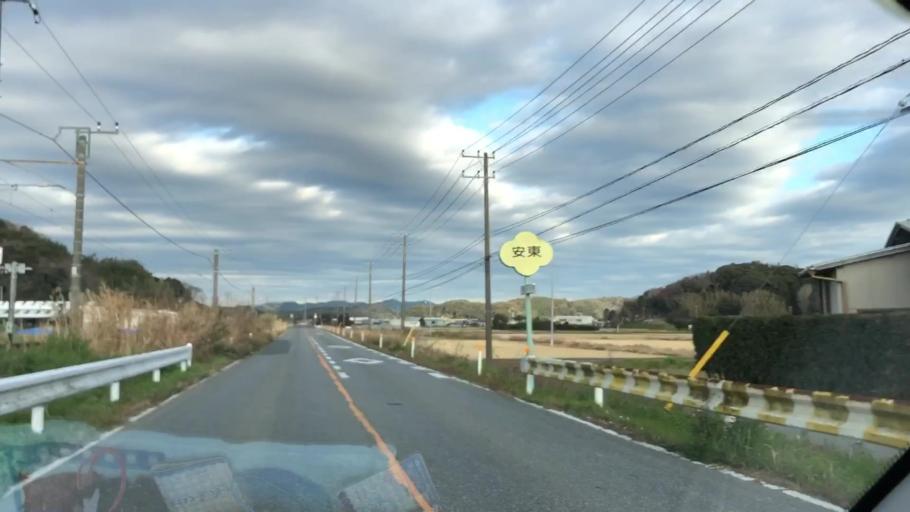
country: JP
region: Chiba
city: Tateyama
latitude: 34.9935
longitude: 139.9202
